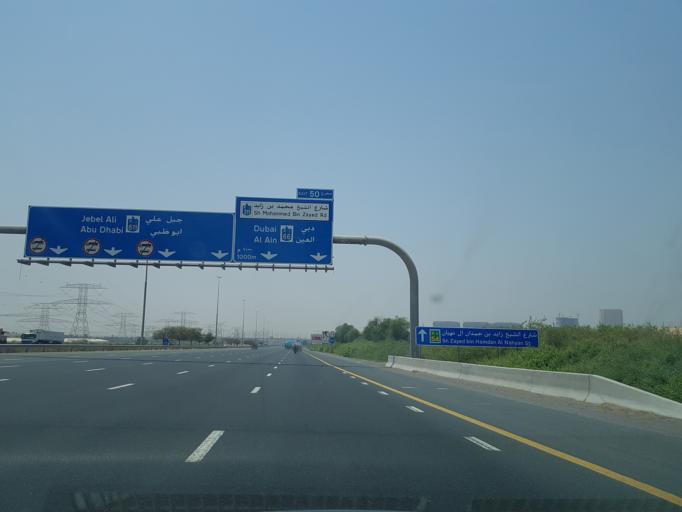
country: AE
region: Dubai
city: Dubai
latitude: 25.0973
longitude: 55.4061
